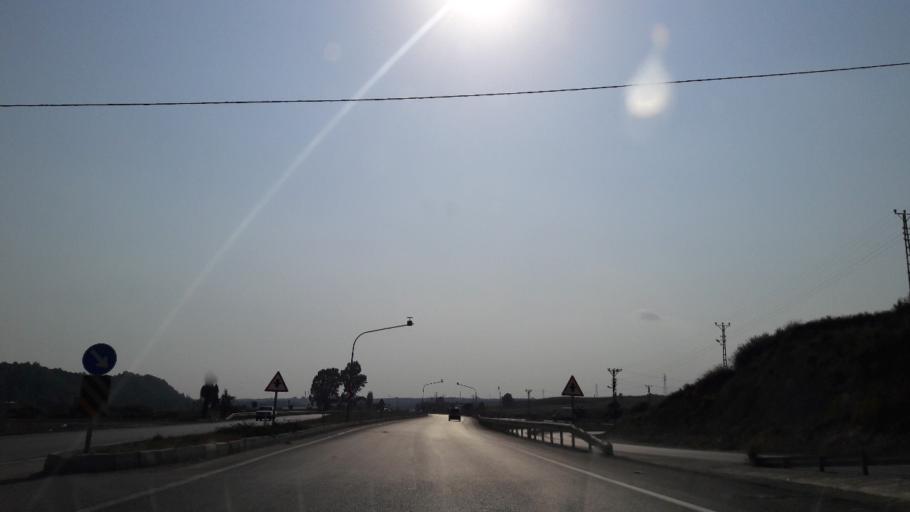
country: TR
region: Adana
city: Yuregir
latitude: 37.0714
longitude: 35.4583
